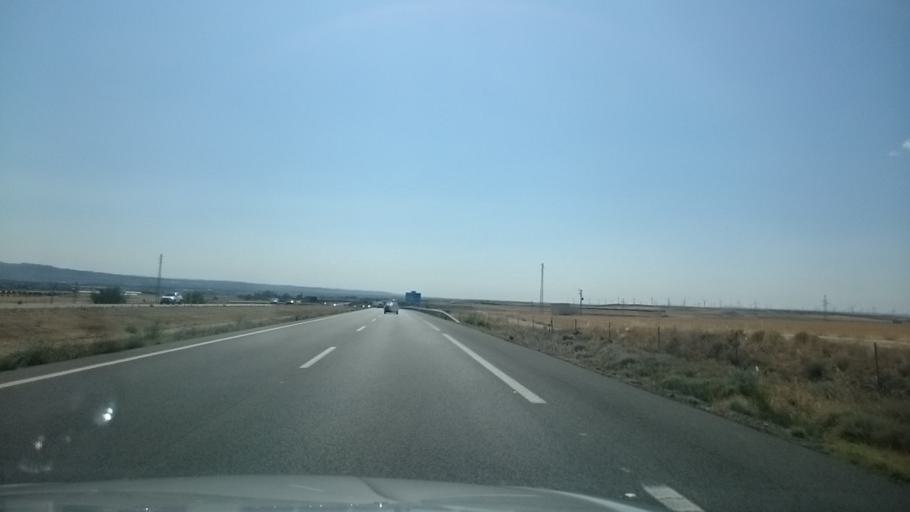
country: ES
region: Aragon
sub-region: Provincia de Zaragoza
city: Gallur
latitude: 41.8368
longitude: -1.3340
